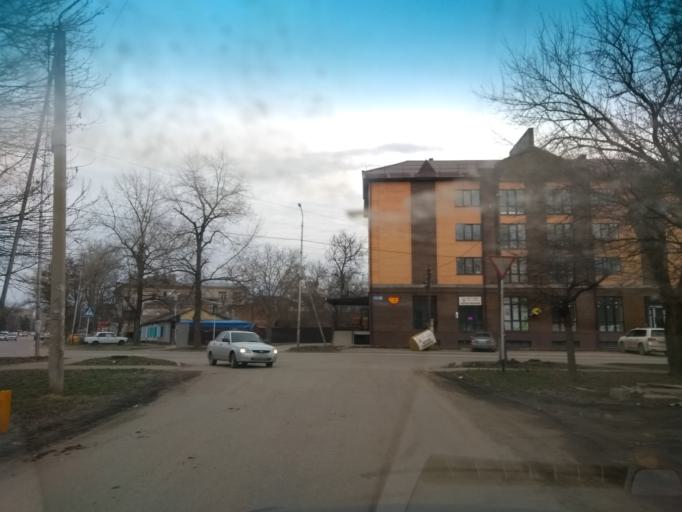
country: RU
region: Stavropol'skiy
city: Georgiyevsk
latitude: 44.1488
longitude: 43.4683
